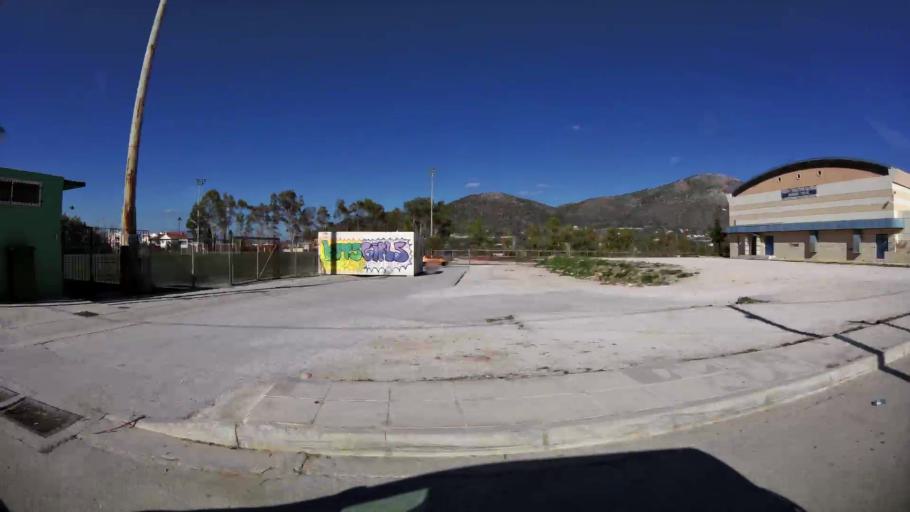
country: GR
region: Attica
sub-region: Nomarchia Anatolikis Attikis
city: Kalyvia Thorikou
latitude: 37.8351
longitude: 23.9339
